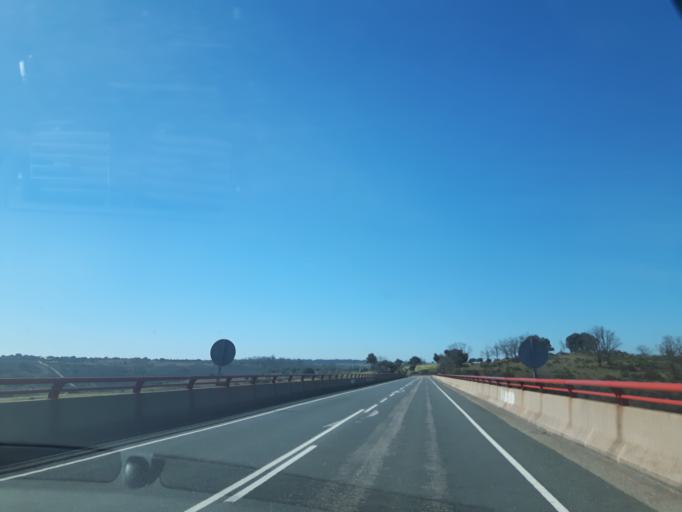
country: ES
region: Castille and Leon
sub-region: Provincia de Salamanca
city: Cerralbo
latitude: 40.9857
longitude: -6.5591
